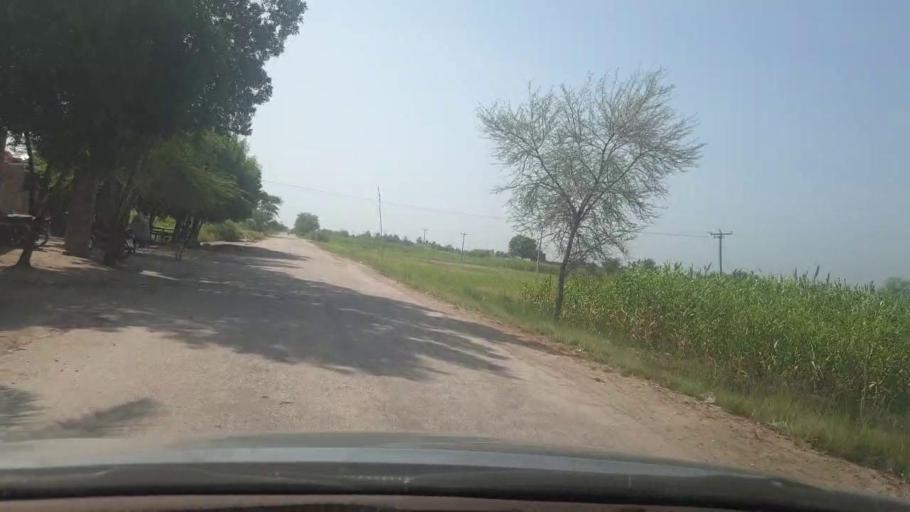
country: PK
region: Sindh
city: Gambat
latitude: 27.3140
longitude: 68.5603
